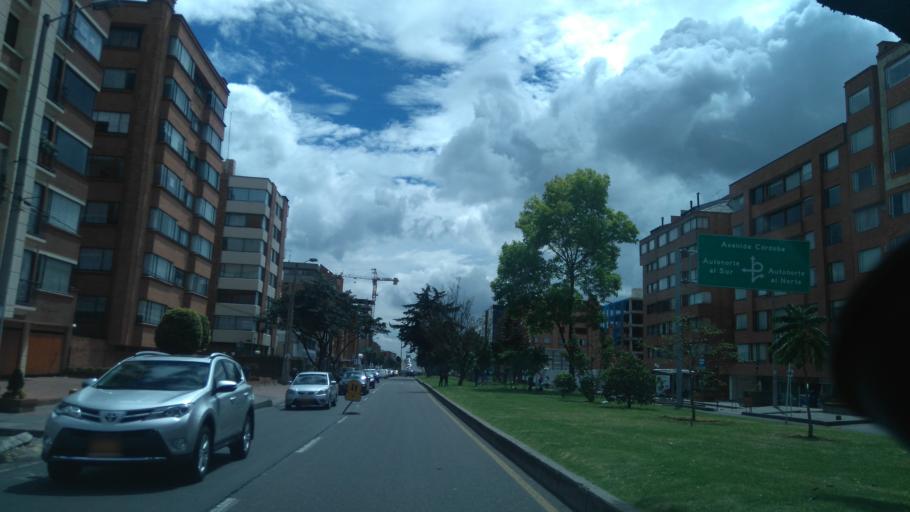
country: CO
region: Bogota D.C.
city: Barrio San Luis
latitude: 4.6989
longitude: -74.0517
